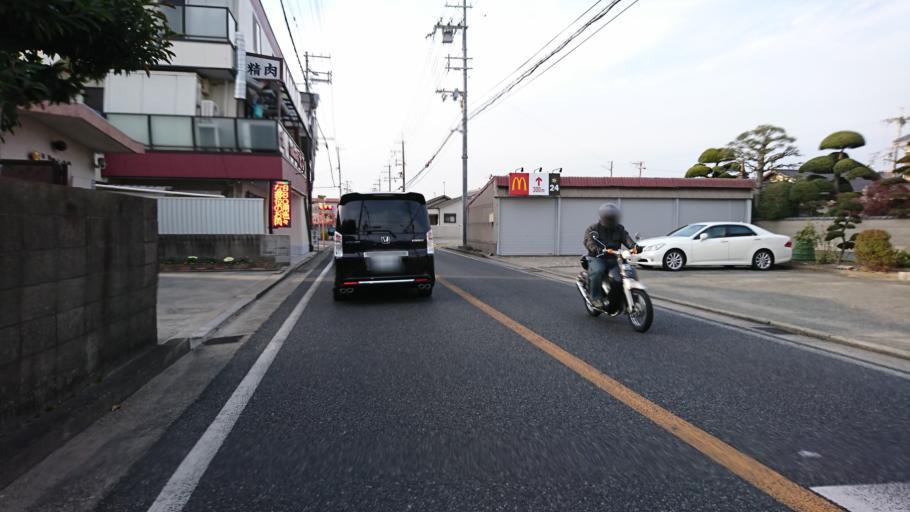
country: JP
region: Hyogo
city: Kakogawacho-honmachi
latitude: 34.7373
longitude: 134.8274
